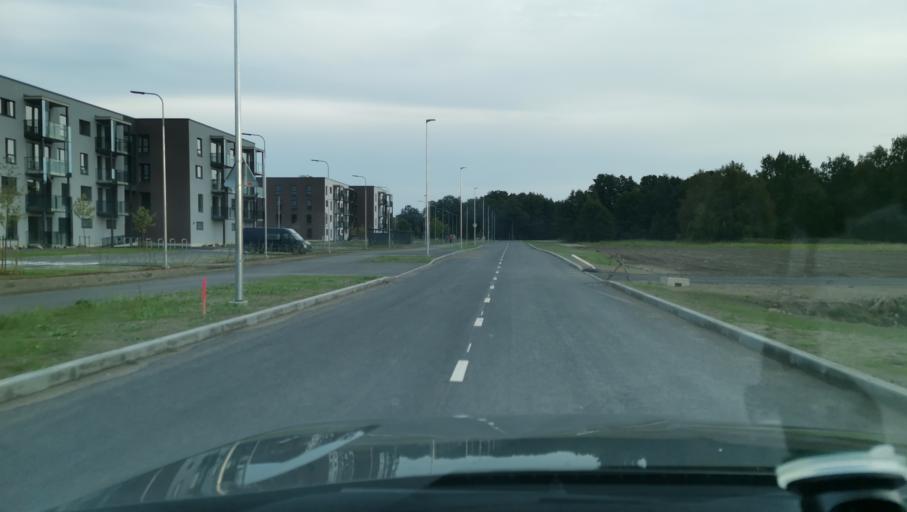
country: EE
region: Harju
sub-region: Saue vald
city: Laagri
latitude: 59.4198
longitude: 24.6296
